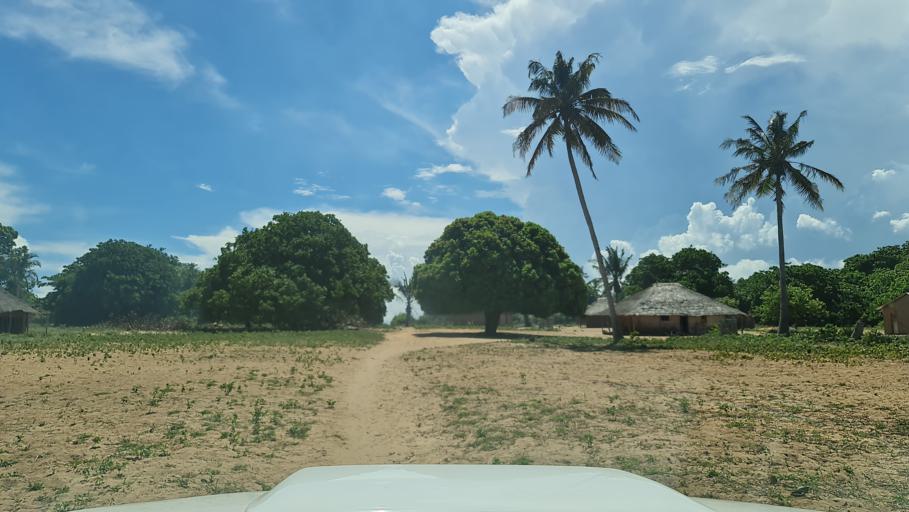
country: MZ
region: Nampula
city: Antonio Enes
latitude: -15.7059
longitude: 40.2612
